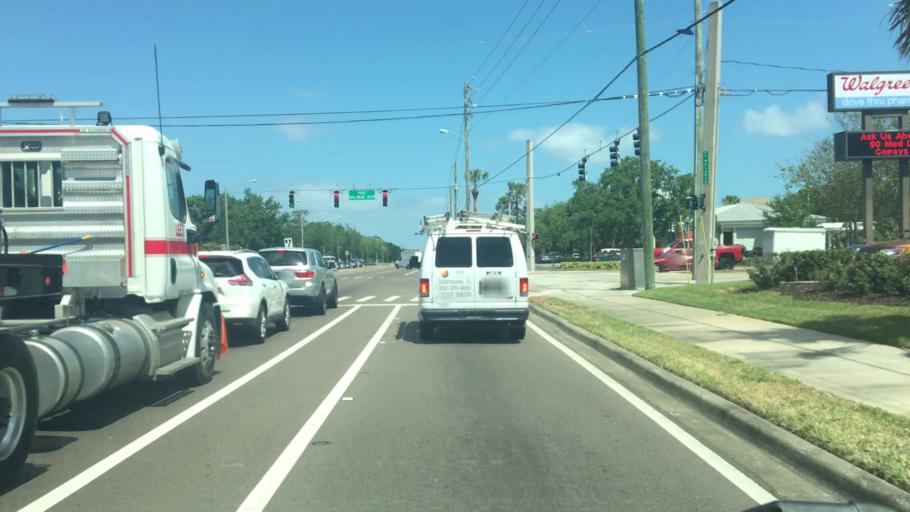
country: US
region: Florida
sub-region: Brevard County
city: Palm Bay
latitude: 28.0188
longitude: -80.6220
